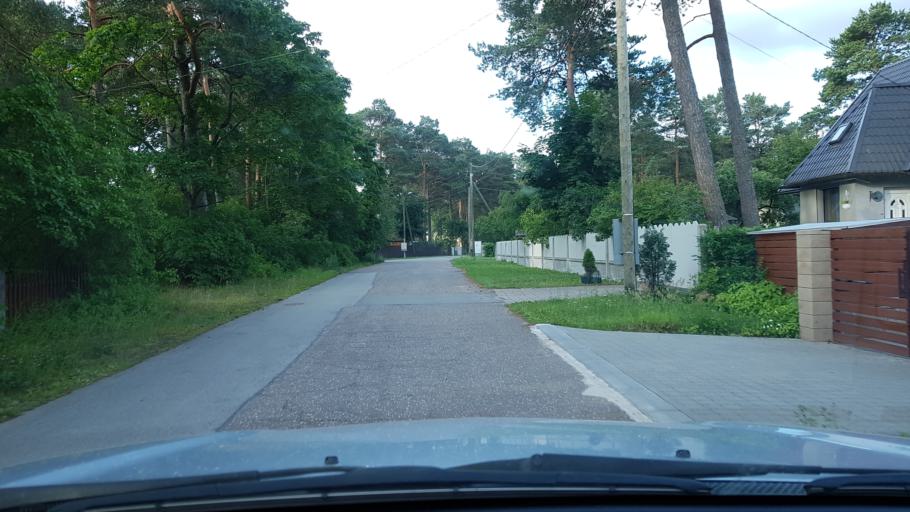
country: EE
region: Ida-Virumaa
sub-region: Narva-Joesuu linn
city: Narva-Joesuu
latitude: 59.4567
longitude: 28.0565
